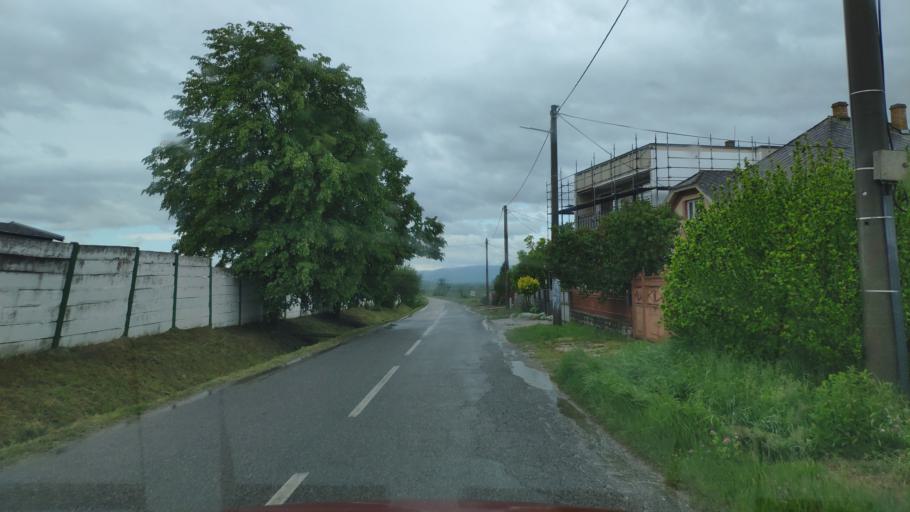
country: SK
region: Kosicky
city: Moldava nad Bodvou
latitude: 48.5356
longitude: 21.0747
